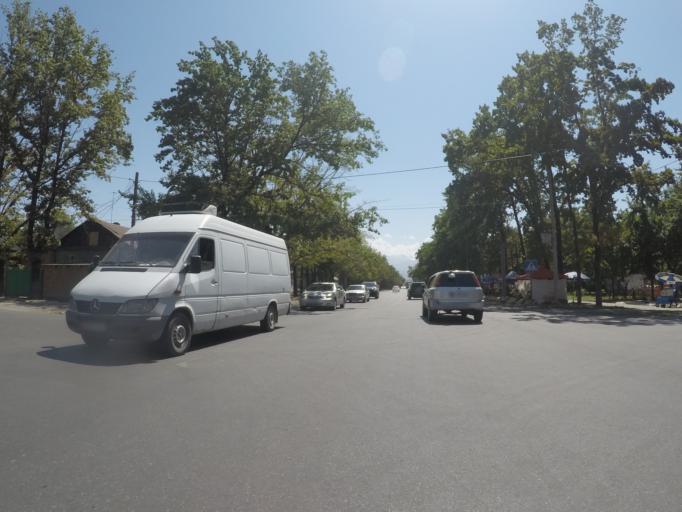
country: KG
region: Chuy
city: Bishkek
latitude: 42.8486
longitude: 74.5770
